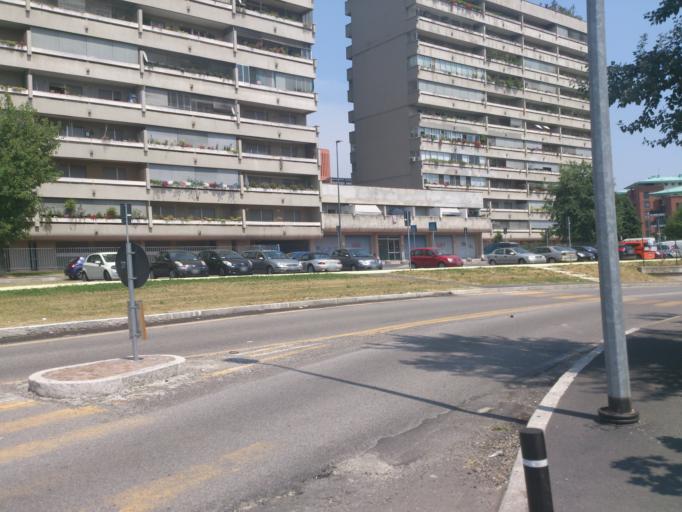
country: IT
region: Lombardy
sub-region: Citta metropolitana di Milano
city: Cologno Monzese
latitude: 45.5190
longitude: 9.2744
